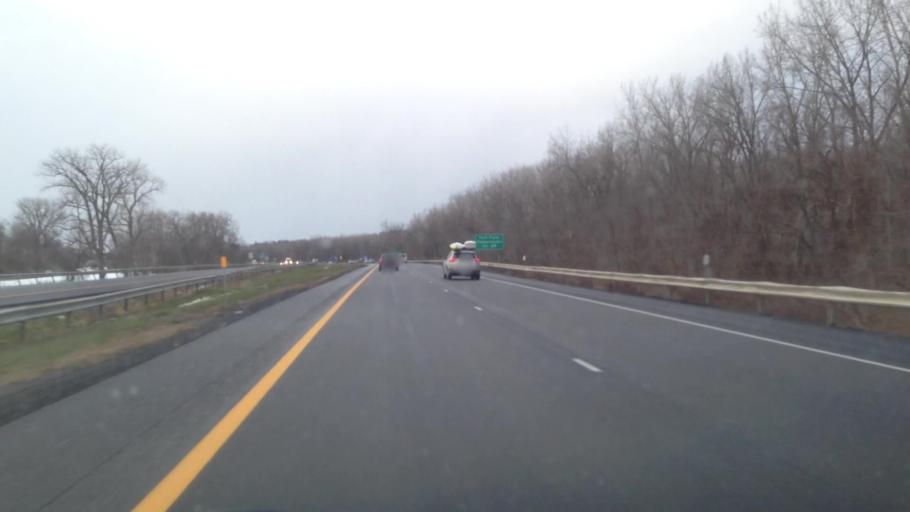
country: US
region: New York
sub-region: Montgomery County
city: Canajoharie
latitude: 42.9001
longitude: -74.5439
